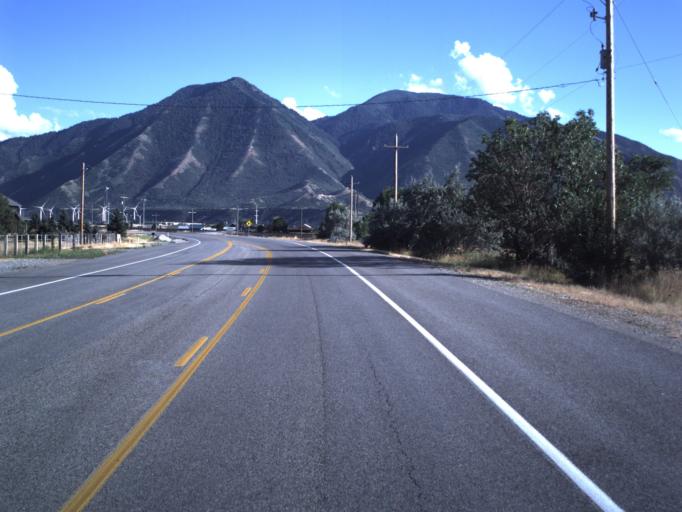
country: US
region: Utah
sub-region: Utah County
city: Mapleton
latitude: 40.1049
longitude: -111.5978
